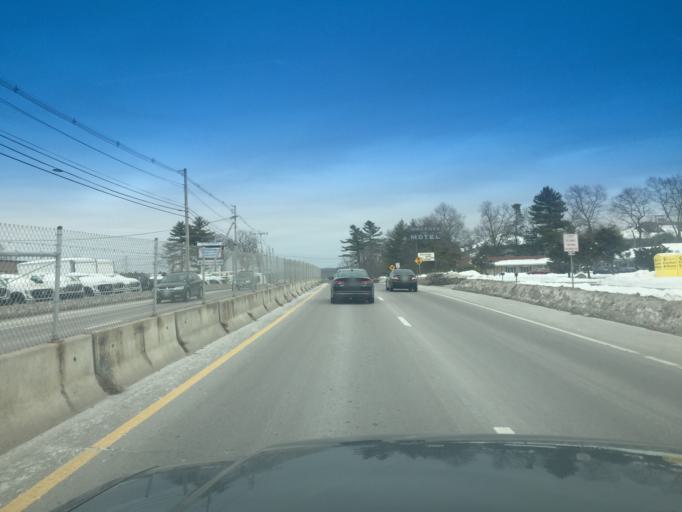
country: US
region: Massachusetts
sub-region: Norfolk County
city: Walpole
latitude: 42.1095
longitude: -71.2464
